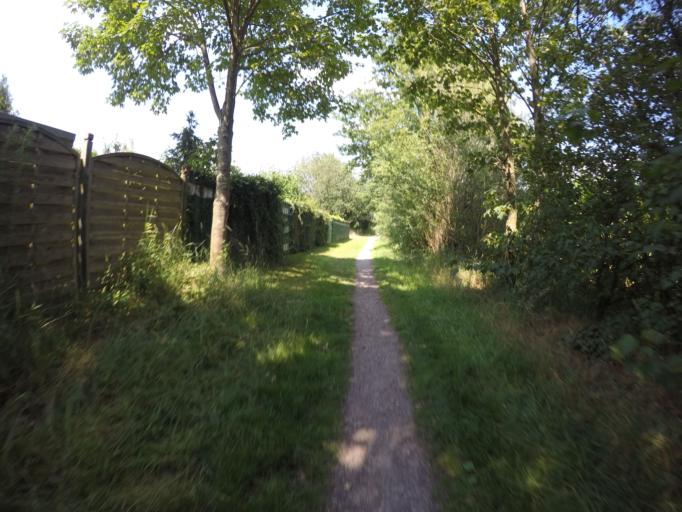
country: DE
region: North Rhine-Westphalia
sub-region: Regierungsbezirk Munster
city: Heiden
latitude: 51.8804
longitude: 6.9185
